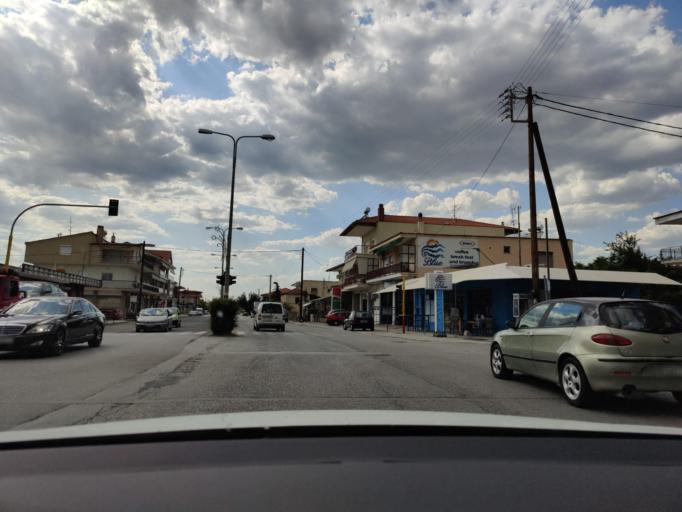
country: GR
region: Central Macedonia
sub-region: Nomos Serron
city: Lefkonas
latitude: 41.0991
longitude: 23.4953
